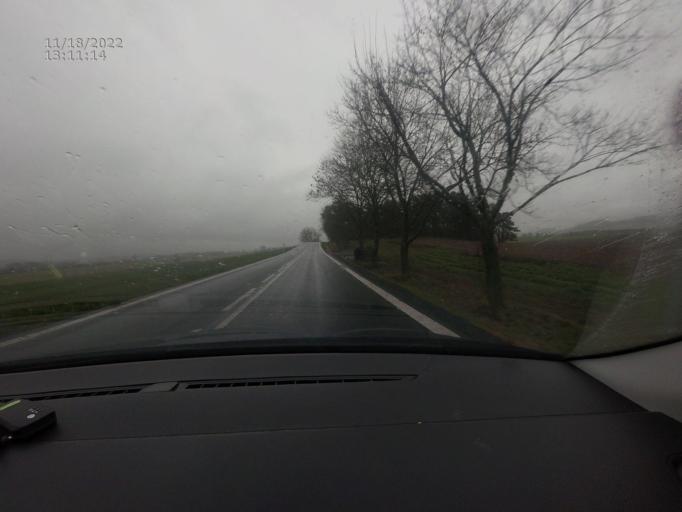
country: CZ
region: Plzensky
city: Hradek
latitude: 49.3285
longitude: 13.5805
